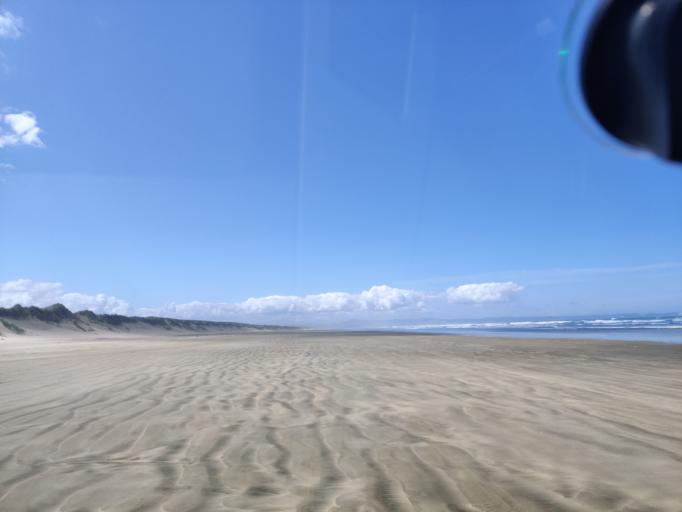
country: NZ
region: Northland
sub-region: Far North District
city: Kaitaia
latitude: -34.9463
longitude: 173.1190
